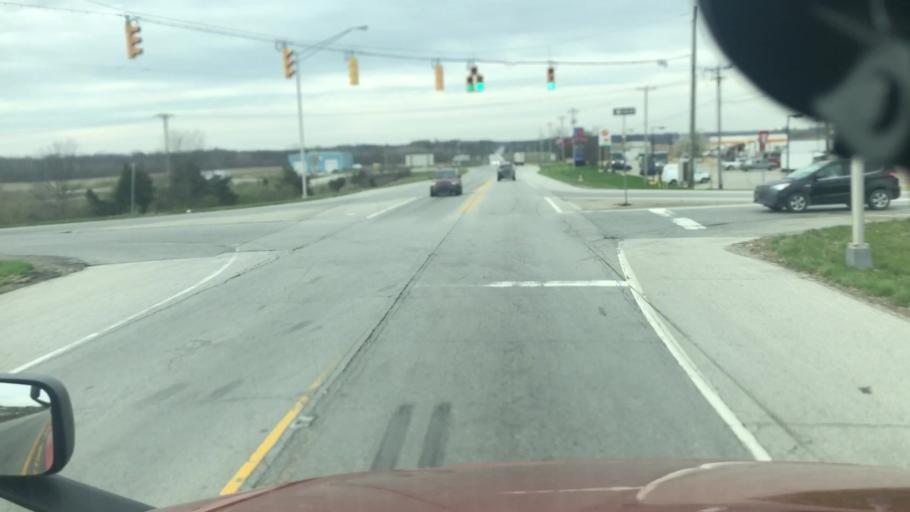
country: US
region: Indiana
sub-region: Morgan County
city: Monrovia
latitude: 39.6128
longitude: -86.4798
